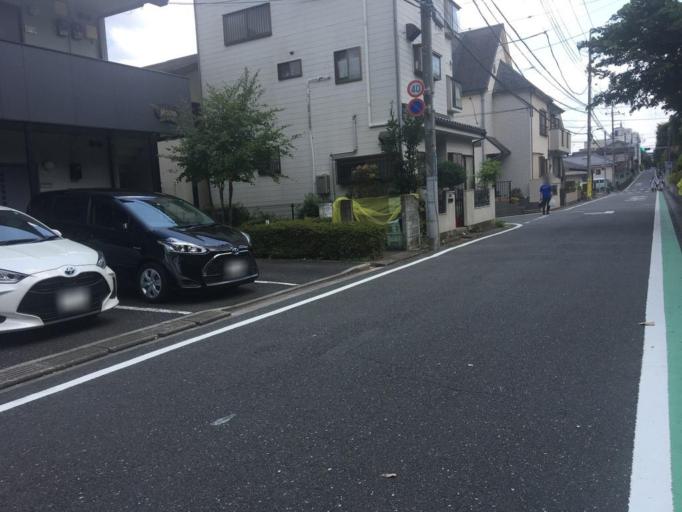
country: JP
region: Saitama
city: Asaka
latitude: 35.7939
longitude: 139.5967
